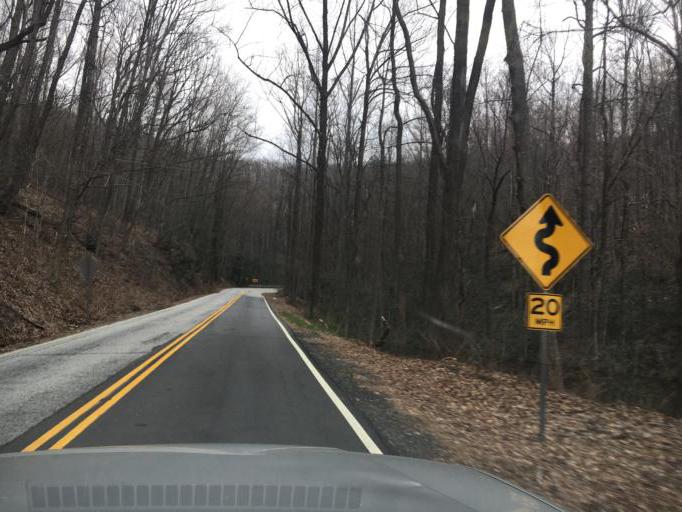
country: US
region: South Carolina
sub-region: Greenville County
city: Slater-Marietta
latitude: 35.1039
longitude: -82.6116
